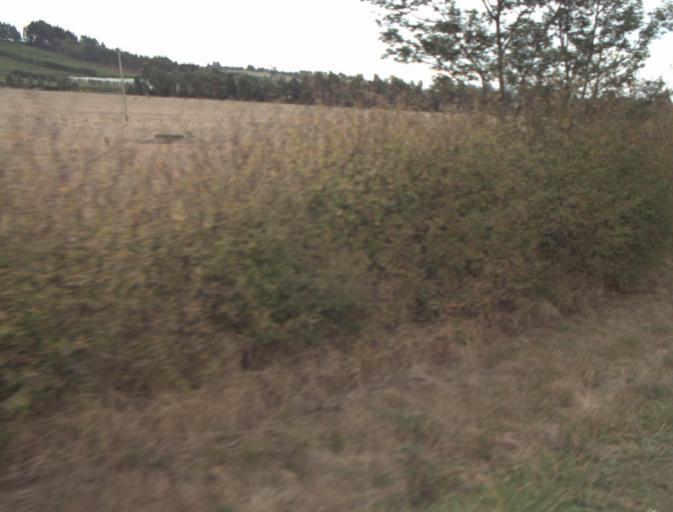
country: AU
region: Tasmania
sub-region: Northern Midlands
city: Evandale
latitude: -41.5100
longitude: 147.2098
